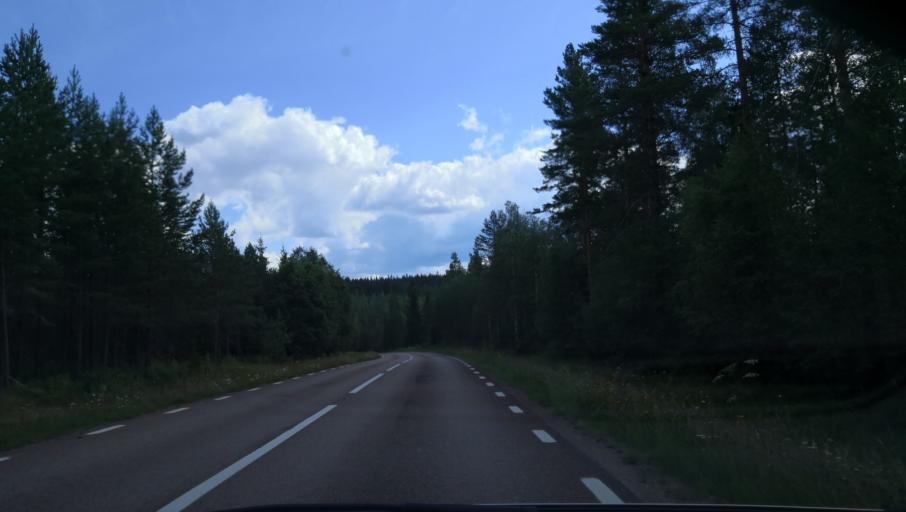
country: SE
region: Dalarna
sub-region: Rattviks Kommun
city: Vikarbyn
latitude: 61.1633
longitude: 15.0111
